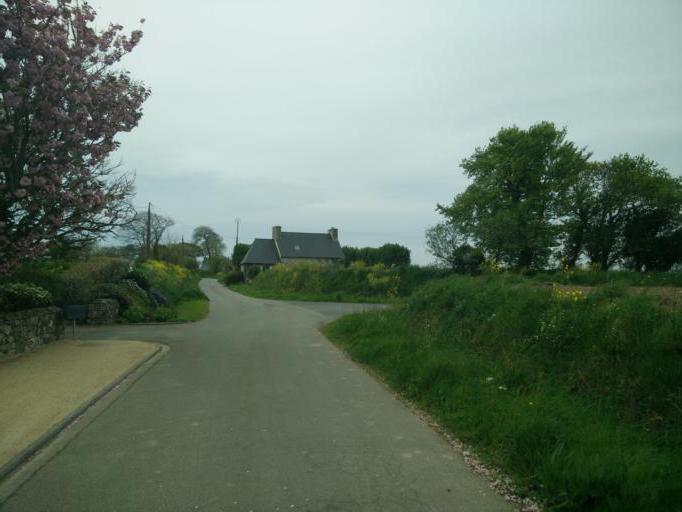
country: FR
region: Brittany
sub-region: Departement des Cotes-d'Armor
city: Tredarzec
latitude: 48.8012
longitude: -3.1975
